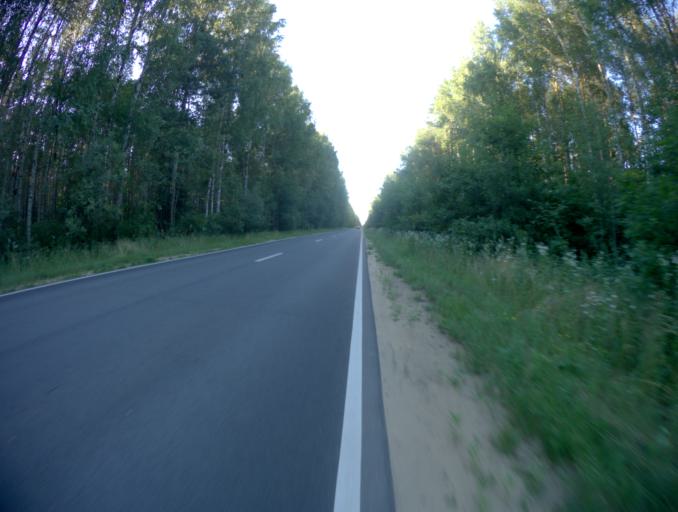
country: RU
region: Vladimir
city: Galitsy
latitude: 56.1057
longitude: 42.8710
